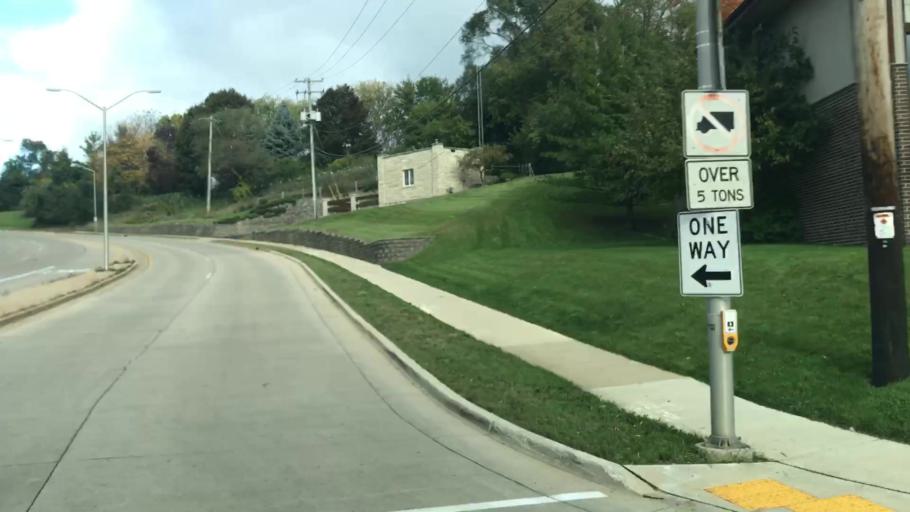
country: US
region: Wisconsin
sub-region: Waukesha County
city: Waukesha
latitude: 43.0229
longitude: -88.2228
